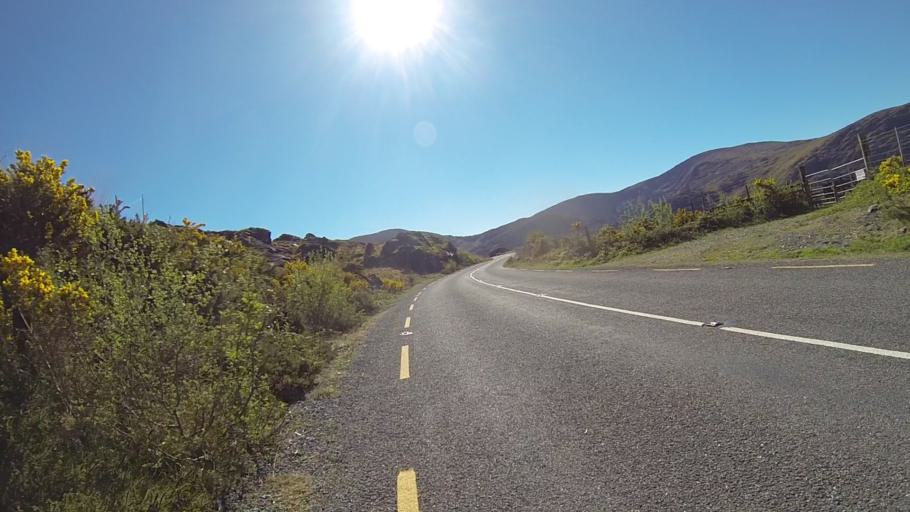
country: IE
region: Munster
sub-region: Ciarrai
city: Kenmare
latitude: 51.7724
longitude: -9.7458
